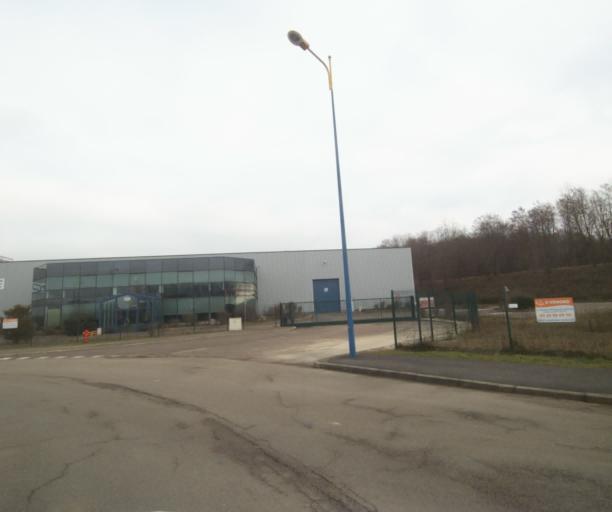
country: FR
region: Champagne-Ardenne
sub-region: Departement de la Haute-Marne
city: Bettancourt-la-Ferree
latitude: 48.6337
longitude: 4.9798
